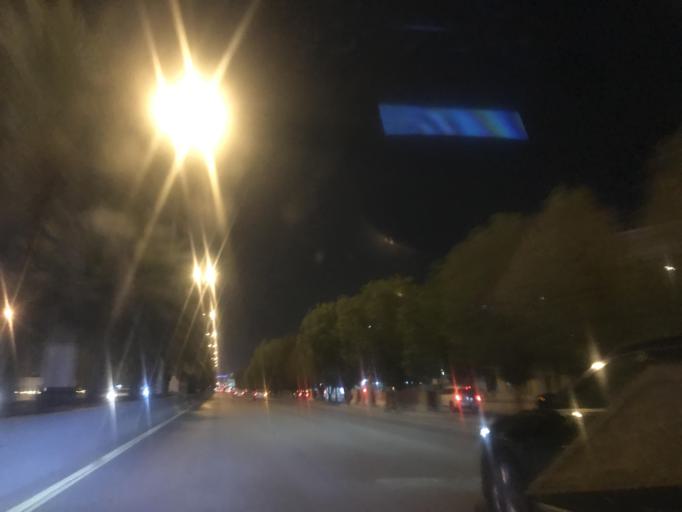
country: SA
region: Ar Riyad
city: Riyadh
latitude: 24.7497
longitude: 46.6679
